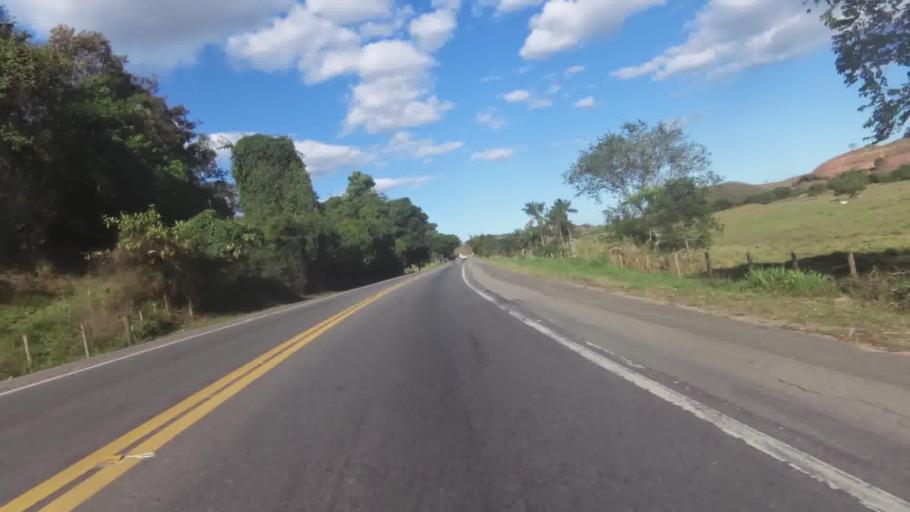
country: BR
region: Espirito Santo
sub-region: Rio Novo Do Sul
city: Rio Novo do Sul
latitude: -20.8744
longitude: -40.9606
